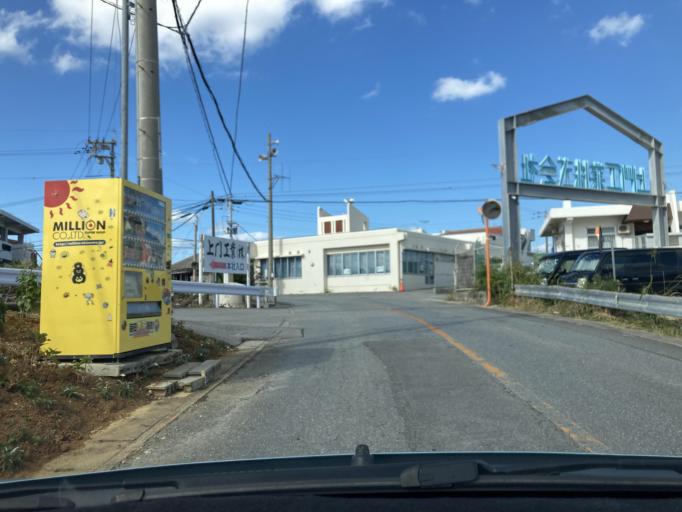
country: JP
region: Okinawa
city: Gushikawa
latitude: 26.3783
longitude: 127.8280
